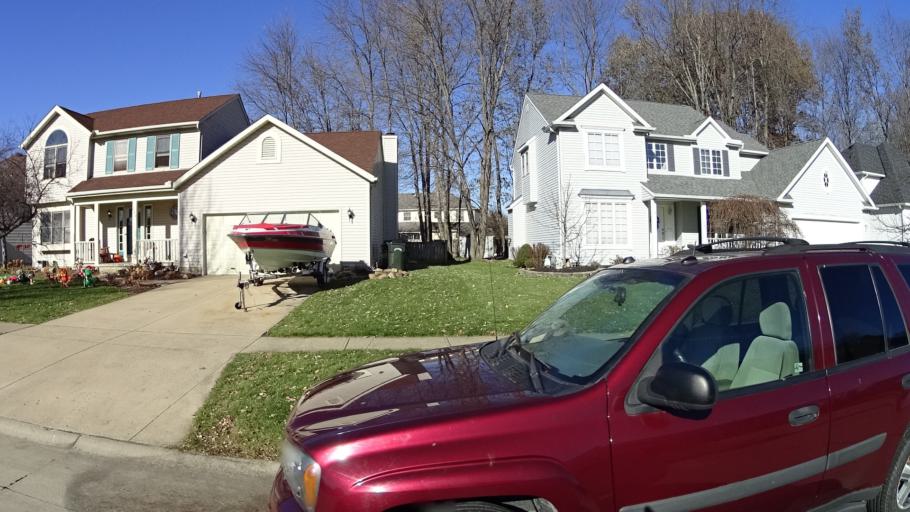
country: US
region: Ohio
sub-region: Lorain County
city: Elyria
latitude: 41.3469
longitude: -82.0862
